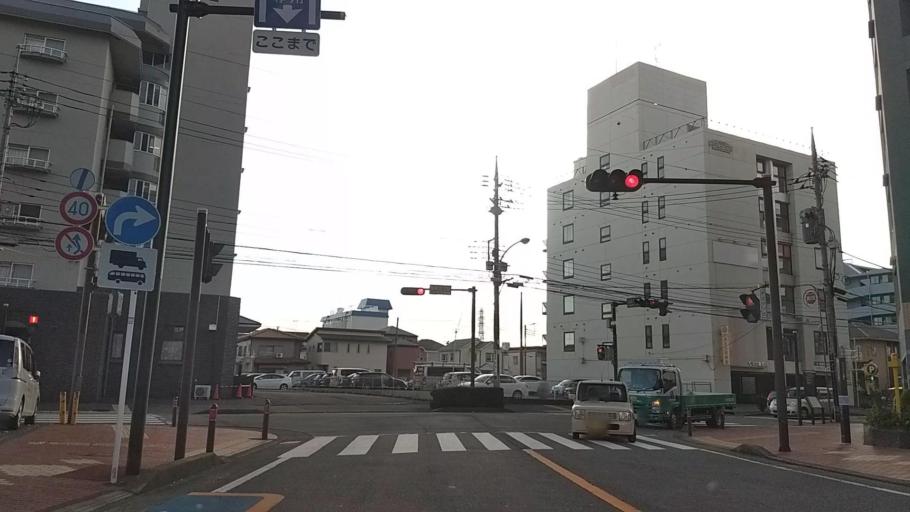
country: JP
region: Kanagawa
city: Atsugi
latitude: 35.4354
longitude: 139.3621
